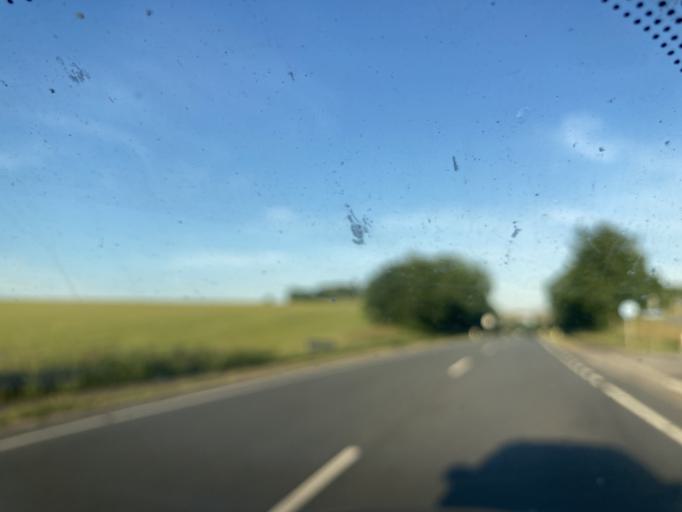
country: DK
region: Zealand
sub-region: Lejre Kommune
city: Lejre
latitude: 55.6376
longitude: 11.9766
